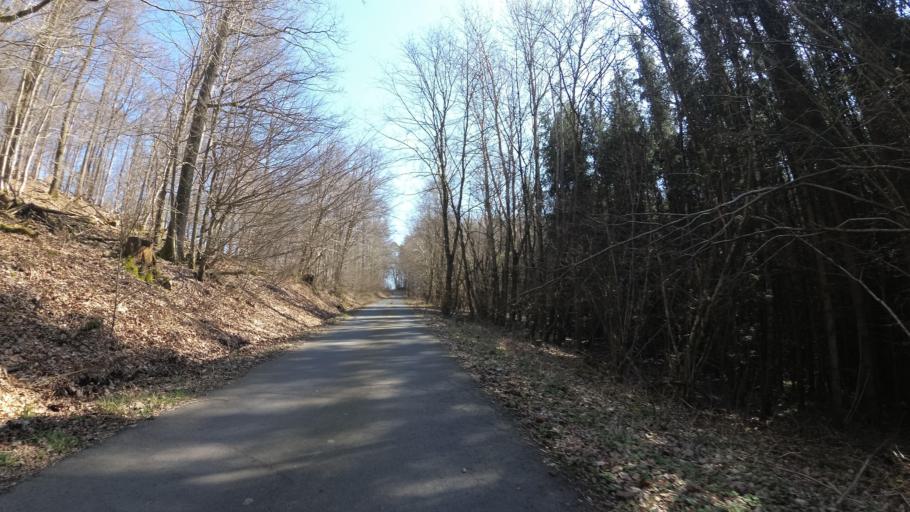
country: DE
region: Rheinland-Pfalz
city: Dambach
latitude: 49.6338
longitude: 7.1253
